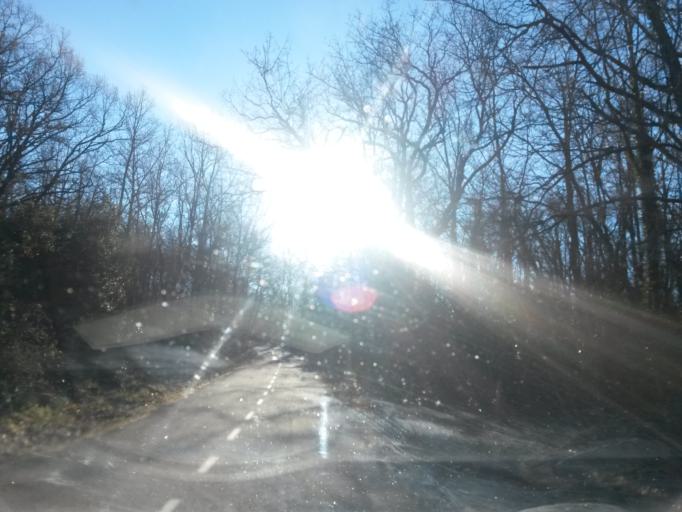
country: ES
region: Catalonia
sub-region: Provincia de Girona
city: les Planes d'Hostoles
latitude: 42.0265
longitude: 2.5337
